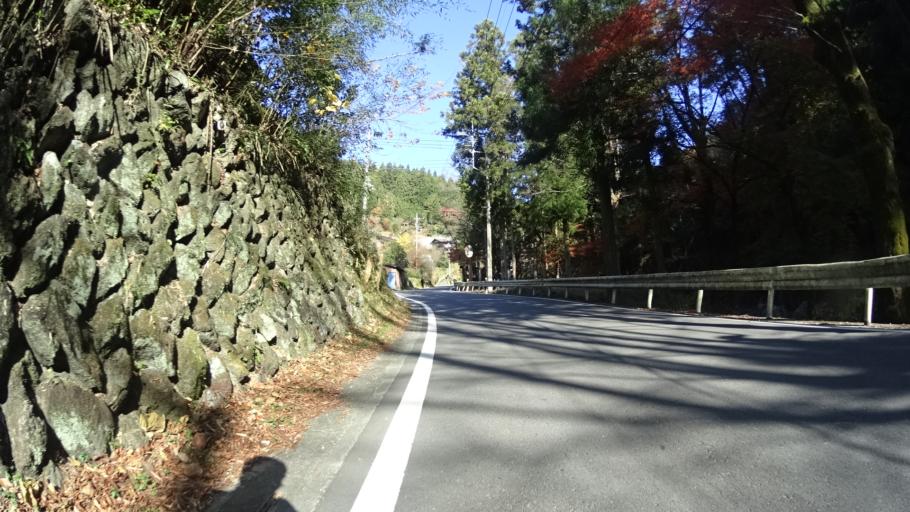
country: JP
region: Saitama
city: Chichibu
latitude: 35.9207
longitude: 139.1510
